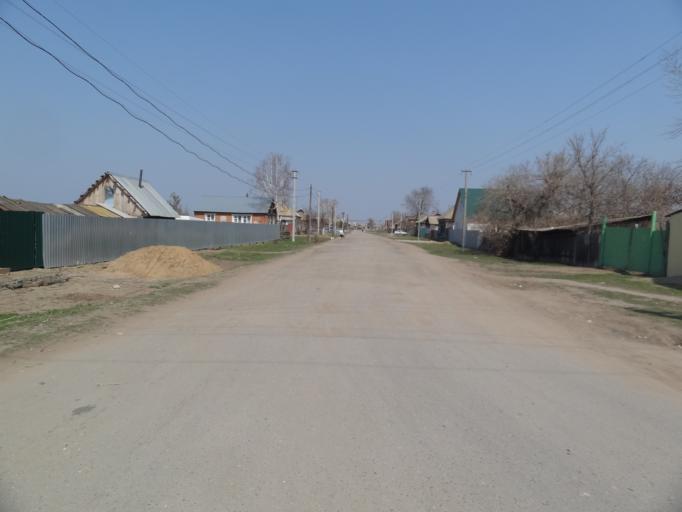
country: RU
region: Saratov
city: Privolzhskiy
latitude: 51.2520
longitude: 45.9148
